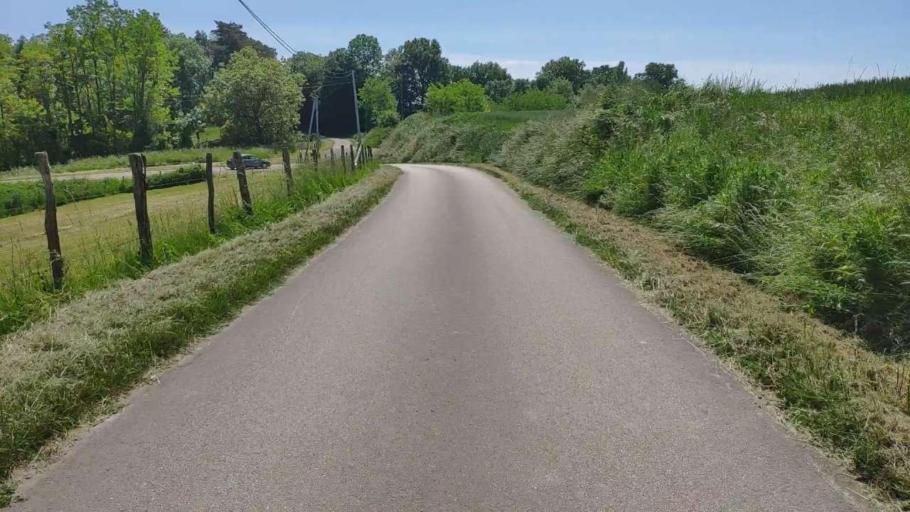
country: FR
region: Franche-Comte
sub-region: Departement du Jura
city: Bletterans
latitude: 46.7453
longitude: 5.3897
